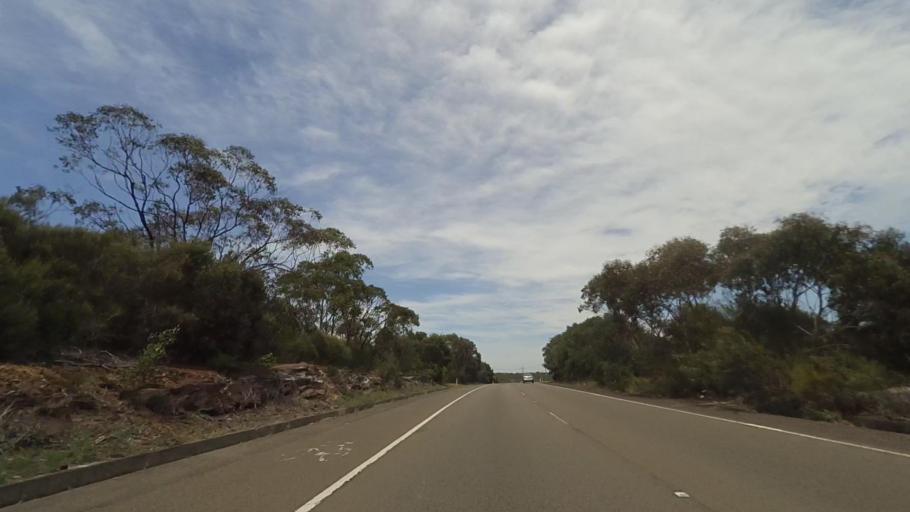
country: AU
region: New South Wales
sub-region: Sutherland Shire
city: Heathcote
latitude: -34.1111
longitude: 150.9931
